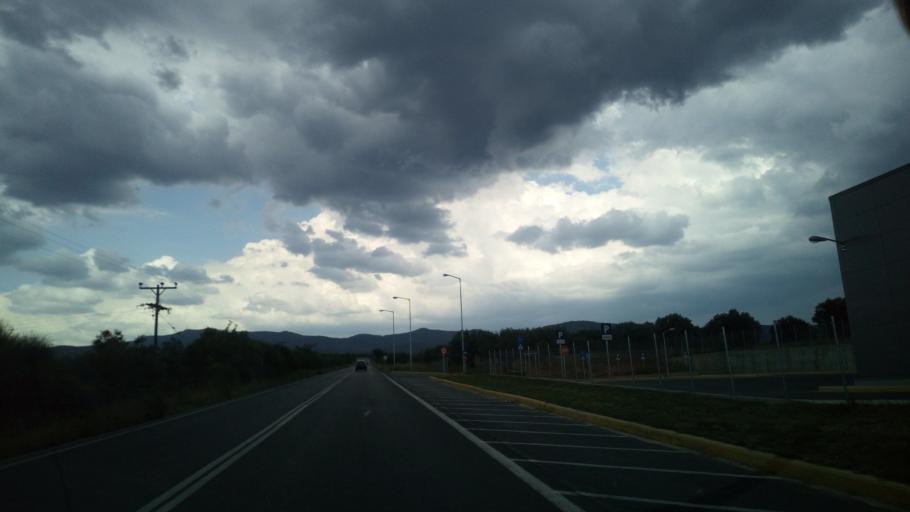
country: GR
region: Central Macedonia
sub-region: Nomos Chalkidikis
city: Kalyves Polygyrou
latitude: 40.3133
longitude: 23.4424
